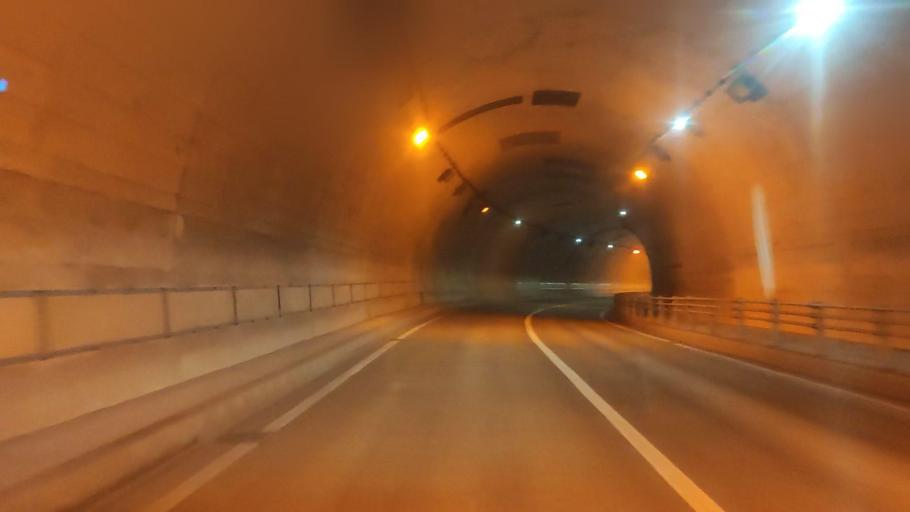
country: JP
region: Kagoshima
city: Kagoshima-shi
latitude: 31.5971
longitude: 130.5491
